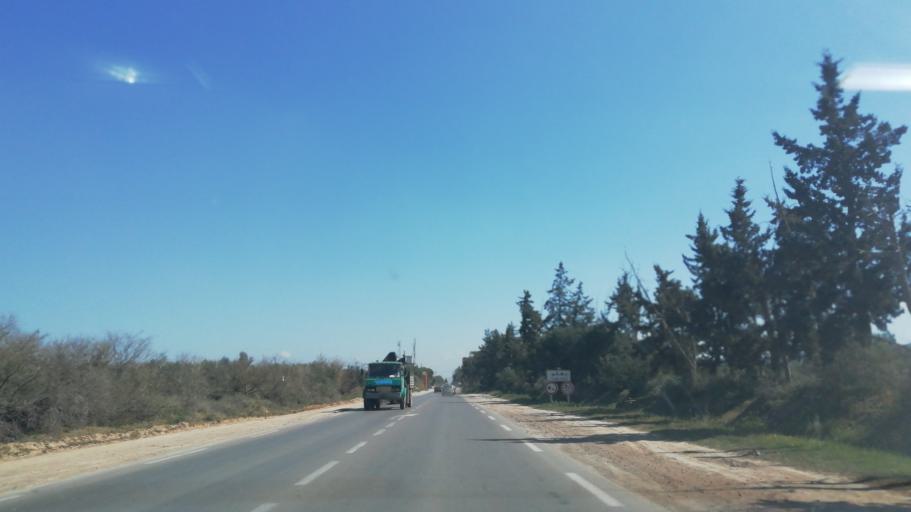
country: DZ
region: Mascara
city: Sig
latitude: 35.5696
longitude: -0.0473
